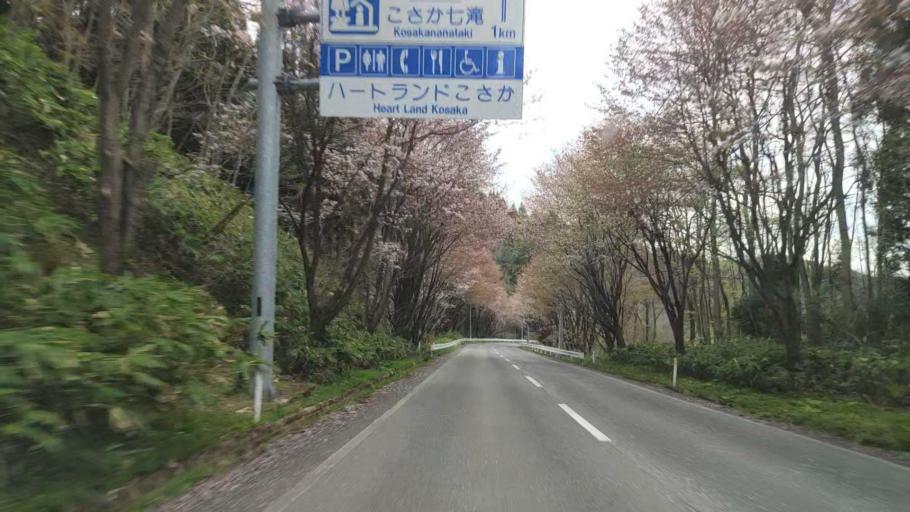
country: JP
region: Akita
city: Hanawa
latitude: 40.3643
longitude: 140.7859
